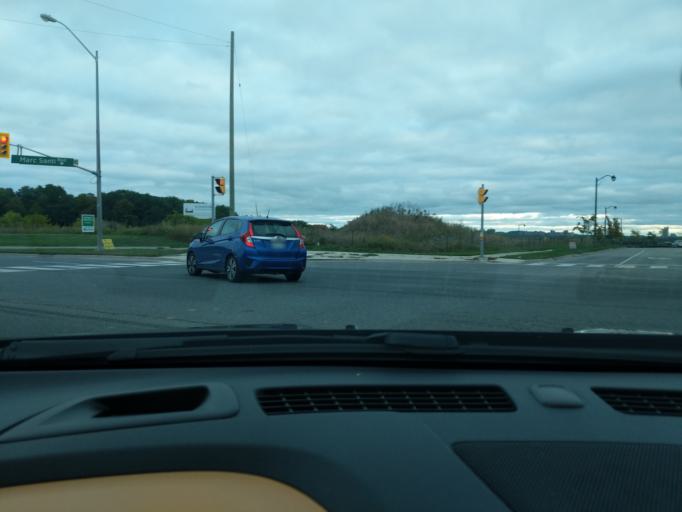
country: CA
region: Ontario
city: Vaughan
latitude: 43.8462
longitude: -79.4840
